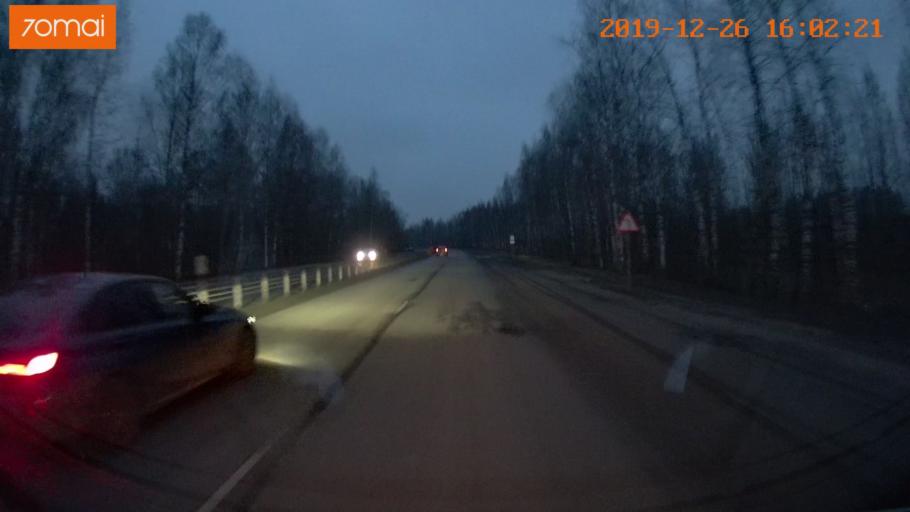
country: RU
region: Jaroslavl
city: Rybinsk
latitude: 58.0123
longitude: 38.8331
